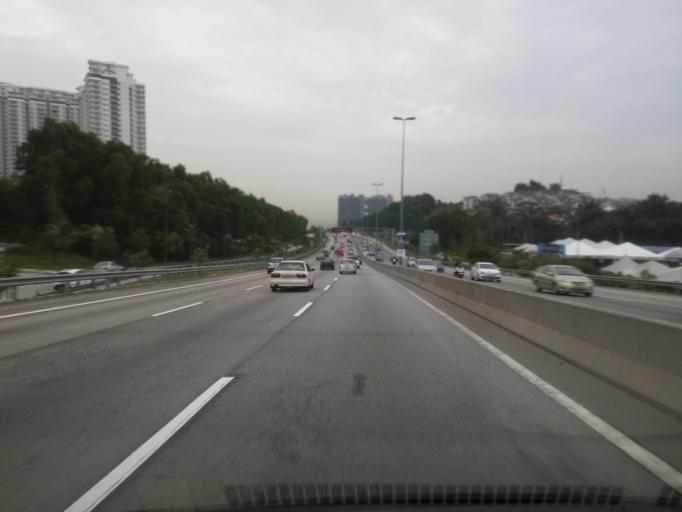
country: MY
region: Kuala Lumpur
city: Kuala Lumpur
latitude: 3.0751
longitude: 101.6894
